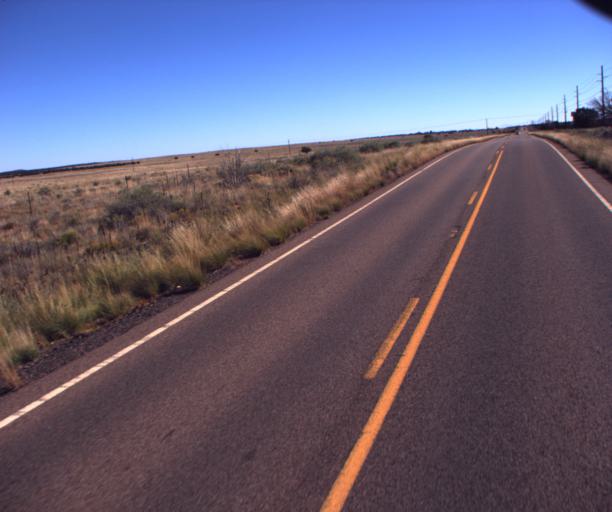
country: US
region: Arizona
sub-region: Navajo County
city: Taylor
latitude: 34.4829
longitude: -110.2853
